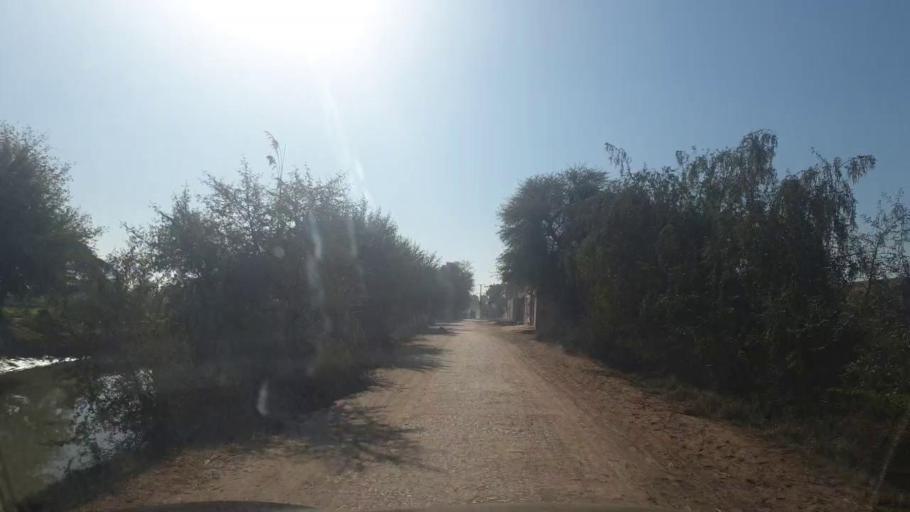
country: PK
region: Sindh
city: Ghotki
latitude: 27.9820
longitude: 69.3263
